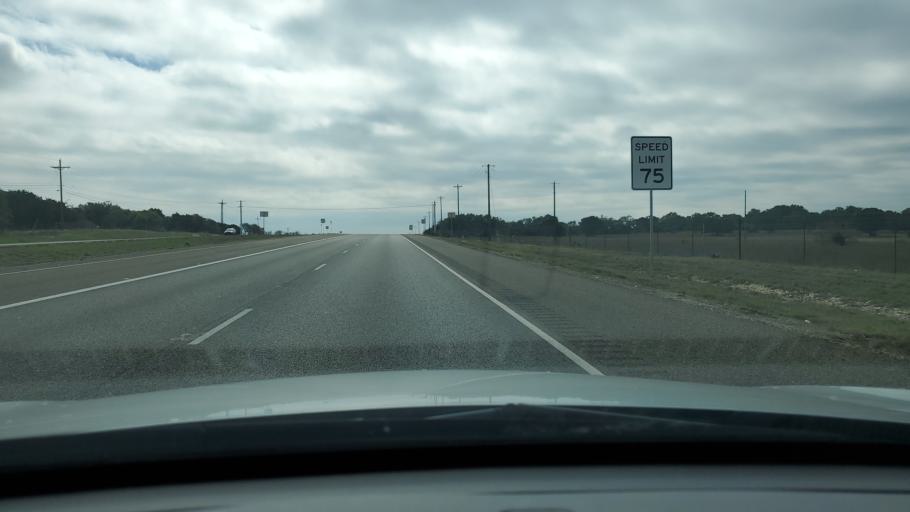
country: US
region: Texas
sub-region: Williamson County
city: Florence
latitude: 30.8092
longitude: -97.7722
